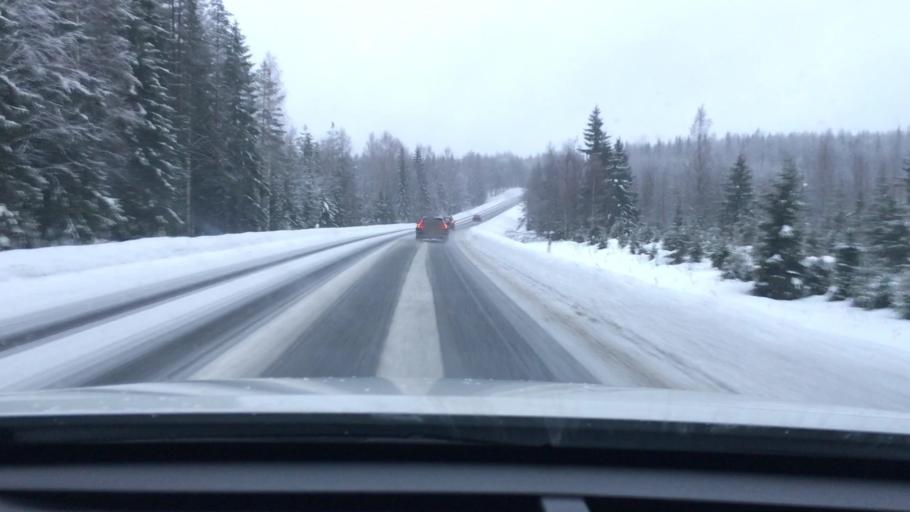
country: FI
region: Northern Savo
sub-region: Ylae-Savo
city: Sonkajaervi
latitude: 63.7704
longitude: 27.4147
